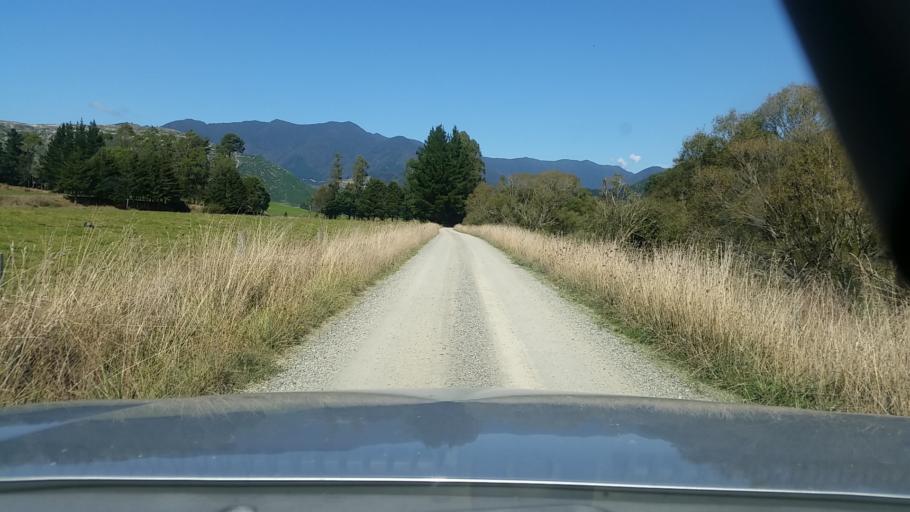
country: NZ
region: Nelson
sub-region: Nelson City
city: Nelson
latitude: -41.2612
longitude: 173.5767
